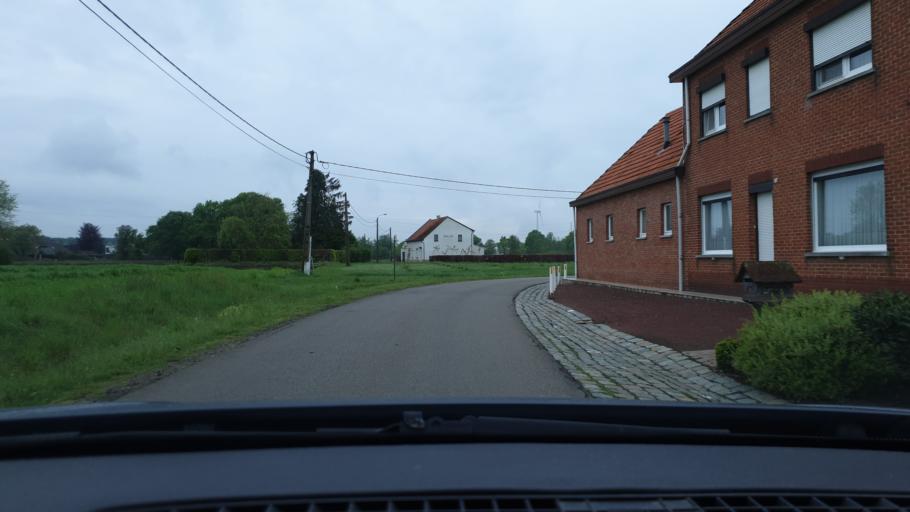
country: BE
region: Flanders
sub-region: Provincie Antwerpen
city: Meerhout
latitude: 51.1200
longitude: 5.0398
